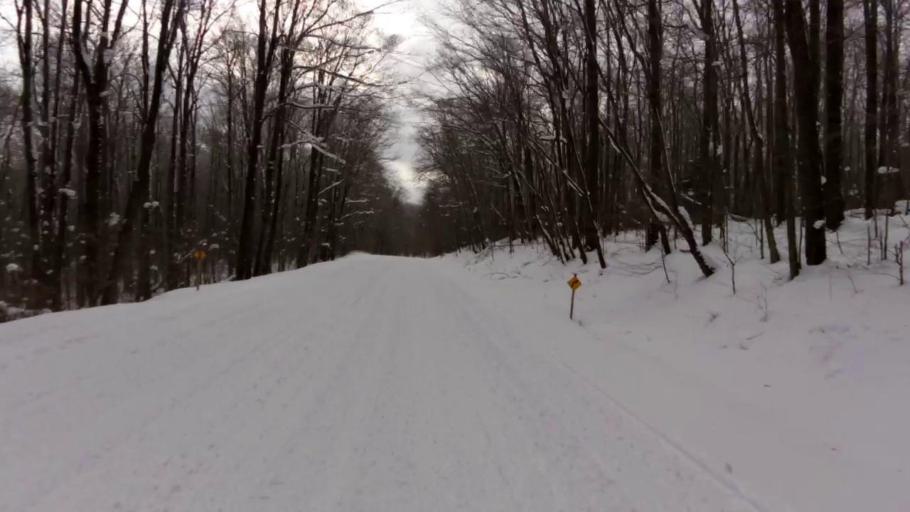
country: US
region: New York
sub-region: Cattaraugus County
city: Salamanca
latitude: 42.0435
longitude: -78.7815
